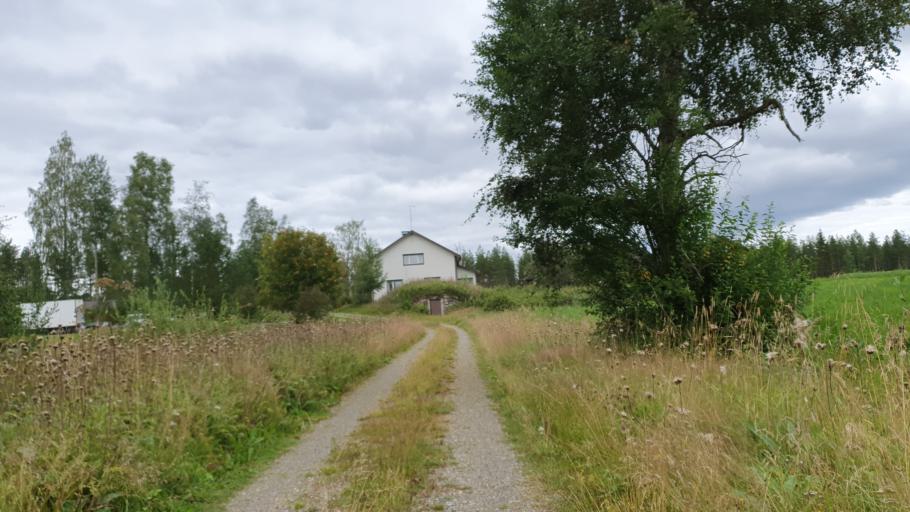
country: FI
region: Kainuu
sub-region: Kehys-Kainuu
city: Kuhmo
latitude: 64.1248
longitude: 29.4587
